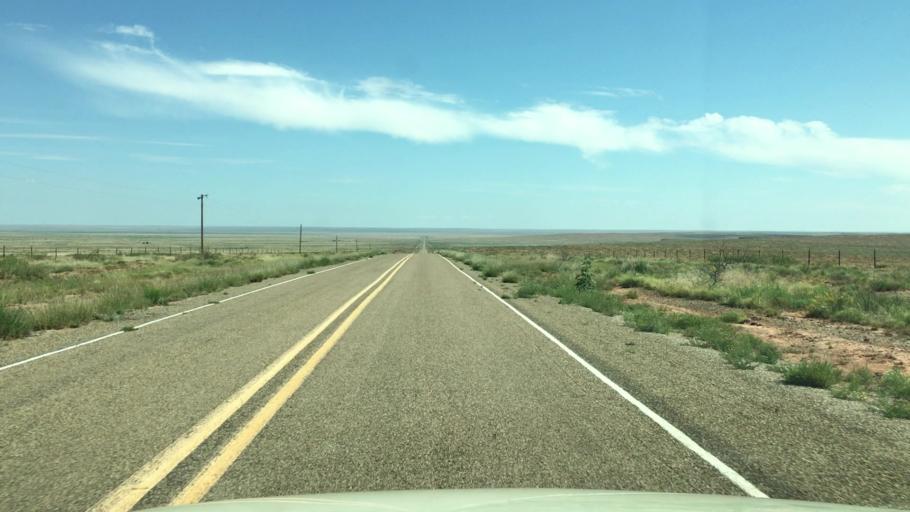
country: US
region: New Mexico
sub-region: Chaves County
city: Roswell
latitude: 33.9669
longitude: -104.5810
